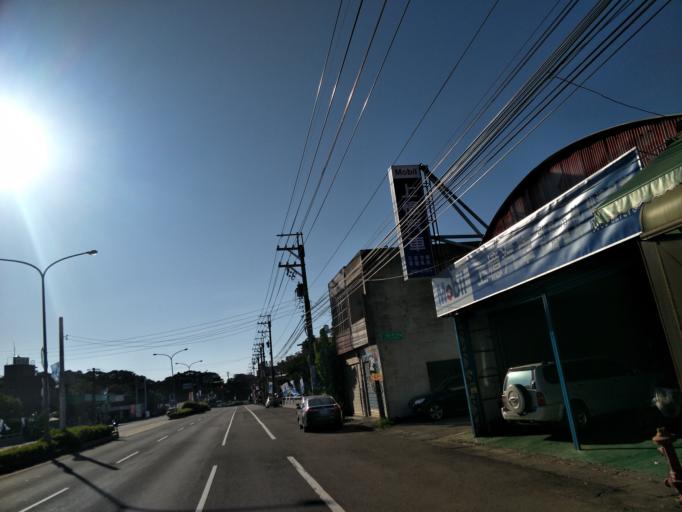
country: TW
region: Taiwan
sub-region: Hsinchu
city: Zhubei
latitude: 24.8778
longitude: 121.0512
